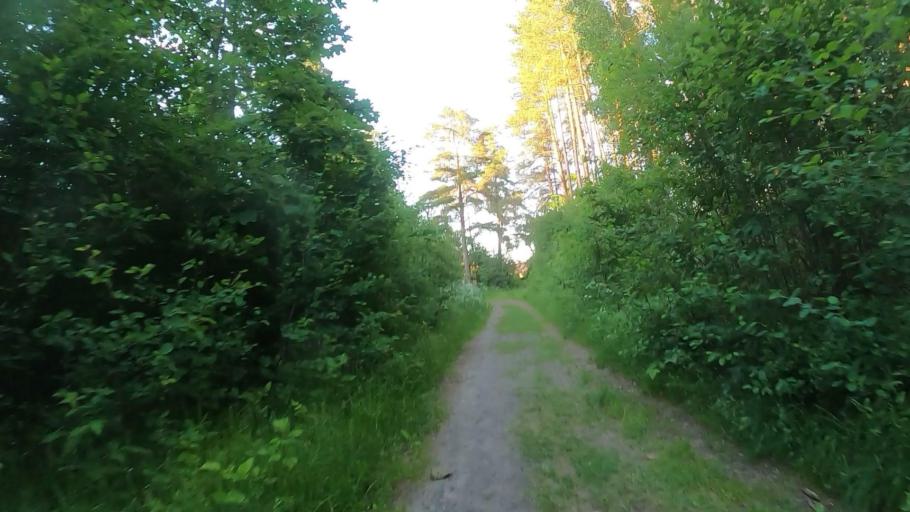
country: LV
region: Marupe
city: Marupe
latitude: 56.8876
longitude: 24.0340
